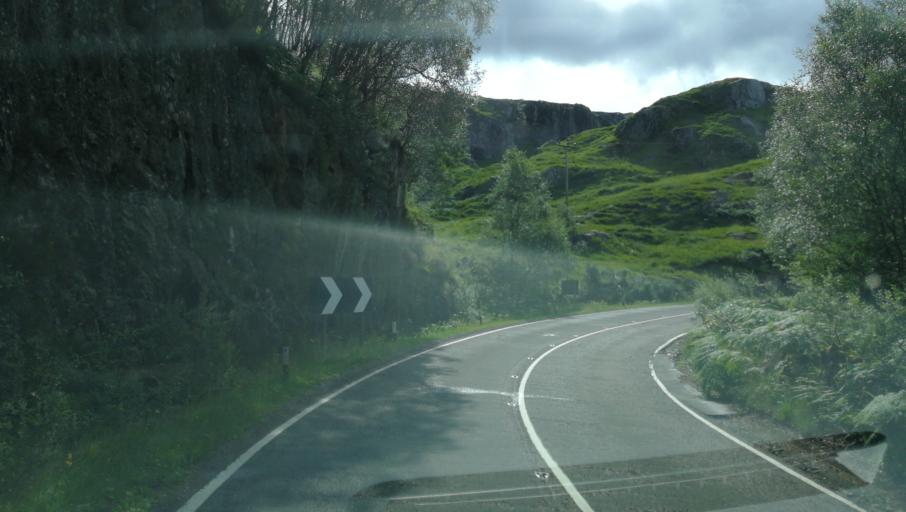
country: GB
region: Scotland
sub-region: Highland
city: Fort William
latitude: 56.8763
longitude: -5.5207
